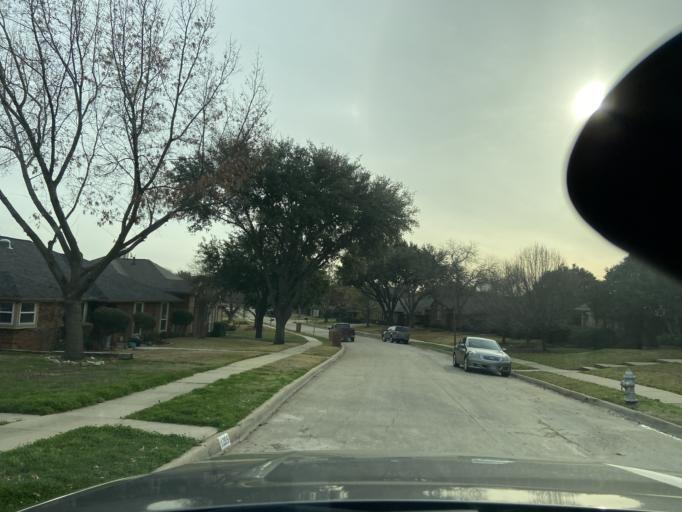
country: US
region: Texas
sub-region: Dallas County
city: Carrollton
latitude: 33.0039
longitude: -96.9065
